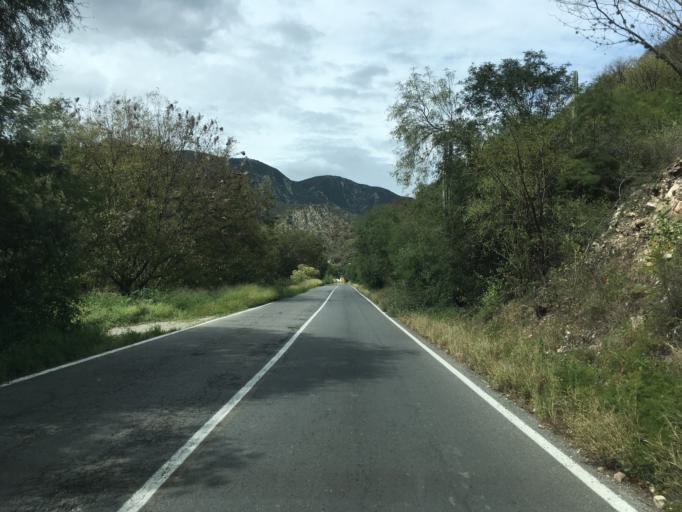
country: MX
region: Hidalgo
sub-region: San Agustin Metzquititlan
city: Mezquititlan
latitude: 20.5216
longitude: -98.7173
